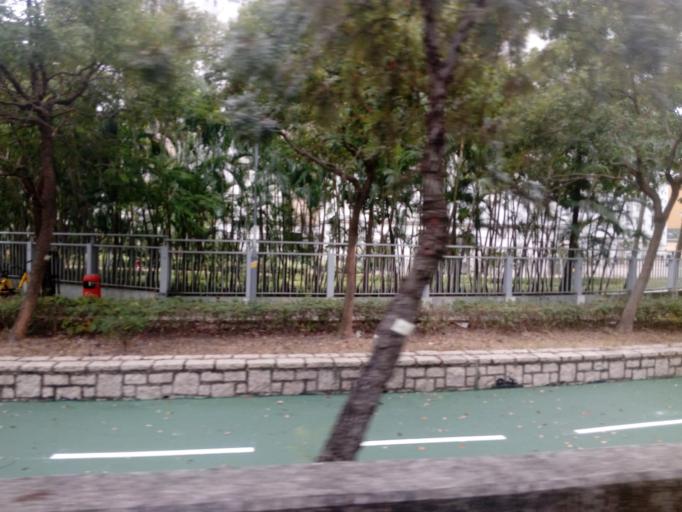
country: HK
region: Yuen Long
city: Yuen Long Kau Hui
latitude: 22.4703
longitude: 114.0019
